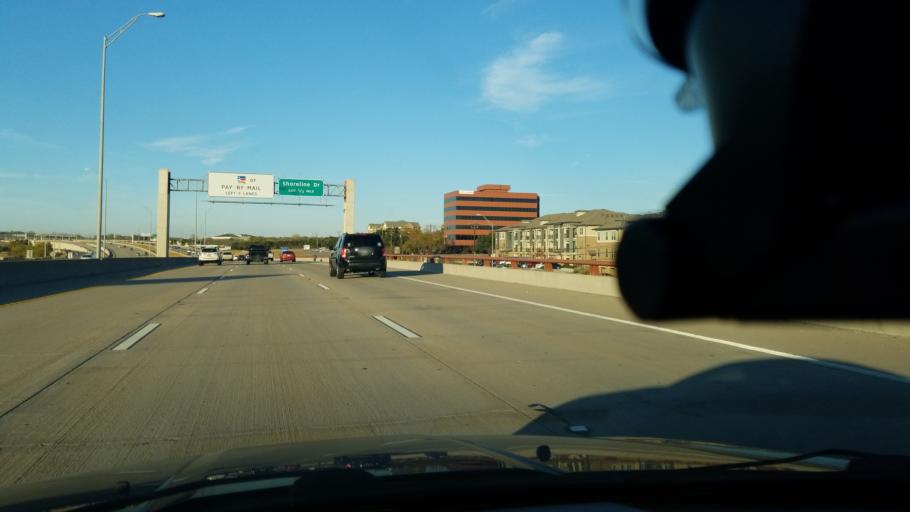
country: US
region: Texas
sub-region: Travis County
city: Wells Branch
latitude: 30.4415
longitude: -97.6977
